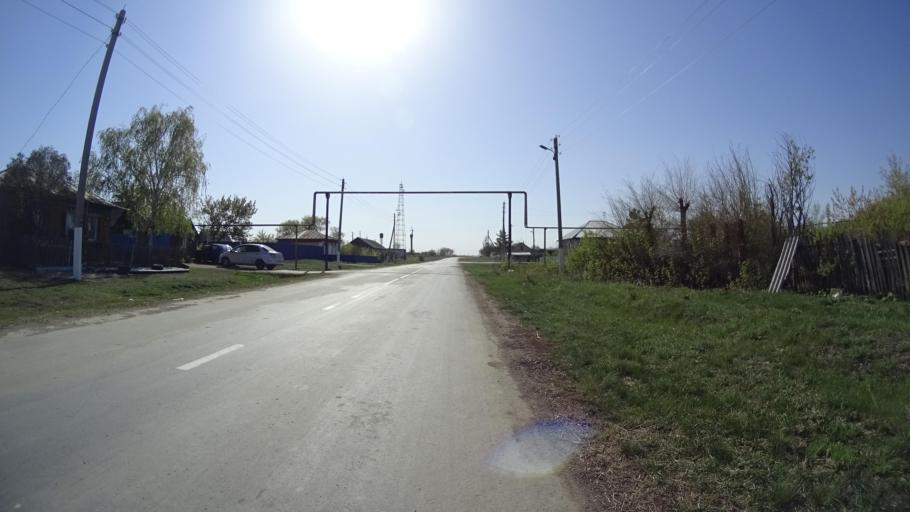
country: RU
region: Chelyabinsk
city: Chesma
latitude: 53.7929
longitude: 61.0365
